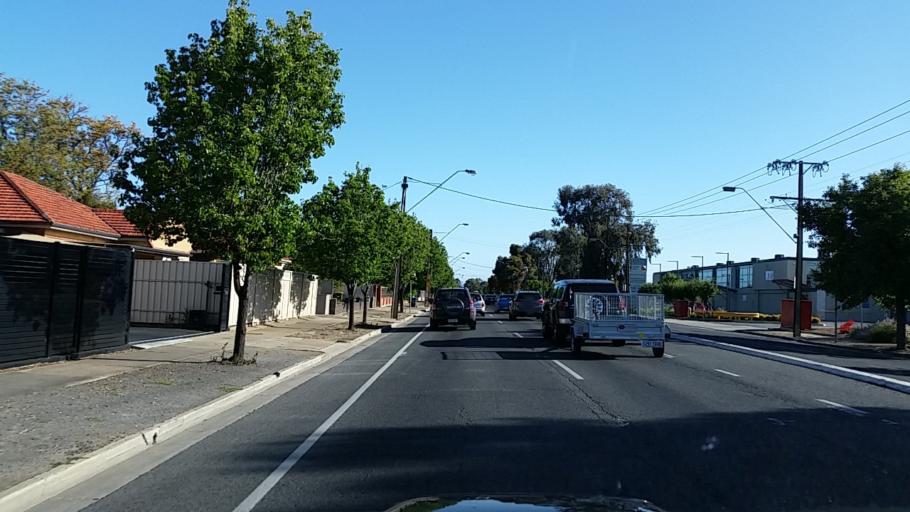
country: AU
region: South Australia
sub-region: City of West Torrens
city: Plympton
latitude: -34.9462
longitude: 138.5535
